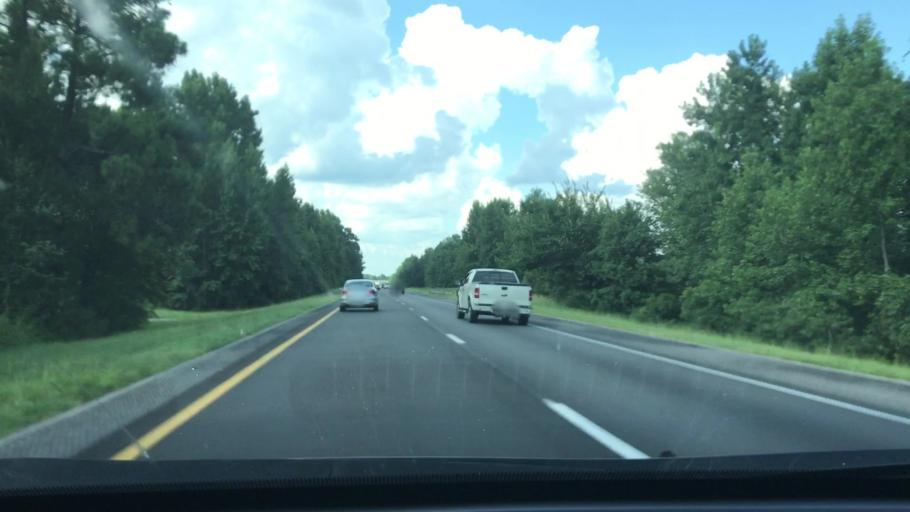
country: US
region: South Carolina
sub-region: Clarendon County
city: Manning
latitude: 33.8496
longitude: -80.1192
